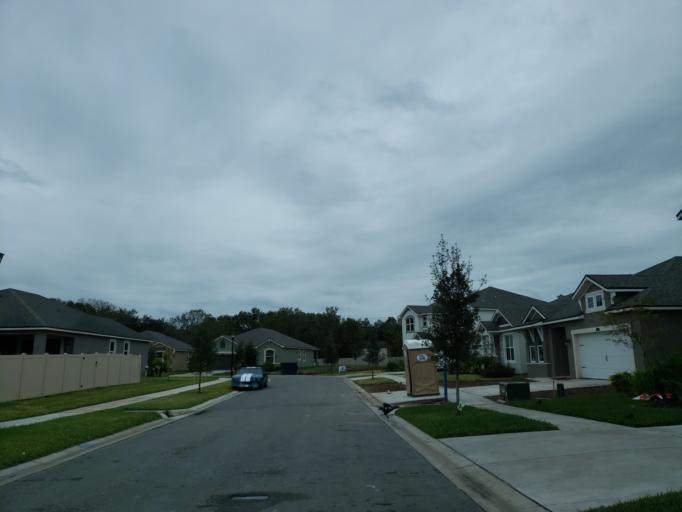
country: US
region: Florida
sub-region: Hillsborough County
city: Riverview
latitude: 27.8474
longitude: -82.3060
